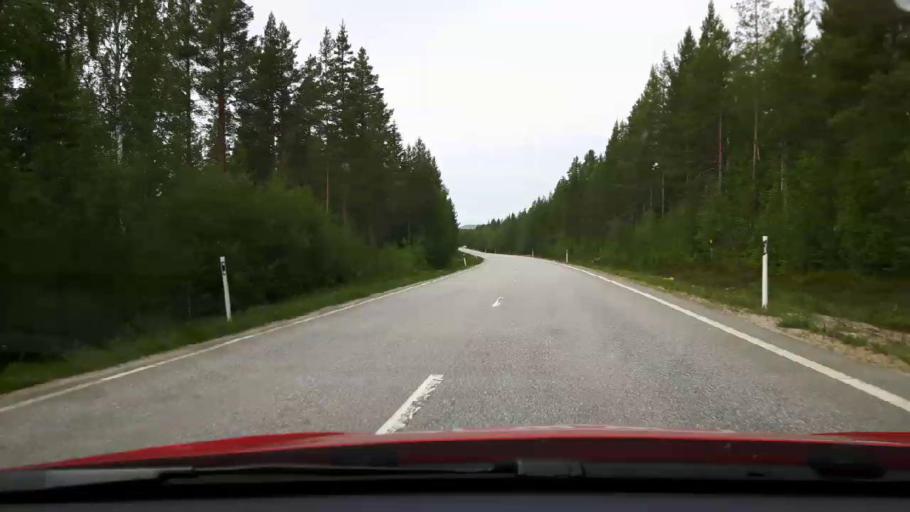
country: SE
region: Jaemtland
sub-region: Harjedalens Kommun
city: Sveg
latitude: 62.1052
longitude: 14.2025
